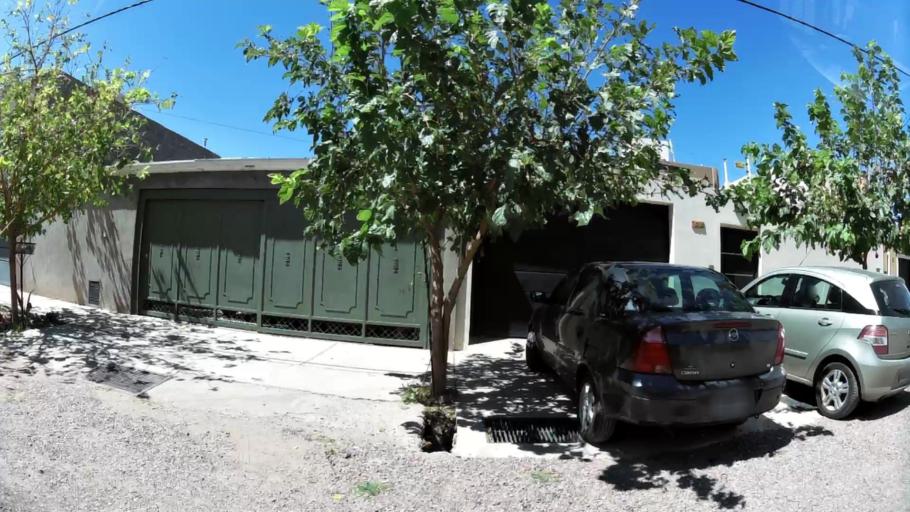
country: AR
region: Mendoza
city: Las Heras
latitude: -32.8455
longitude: -68.8517
